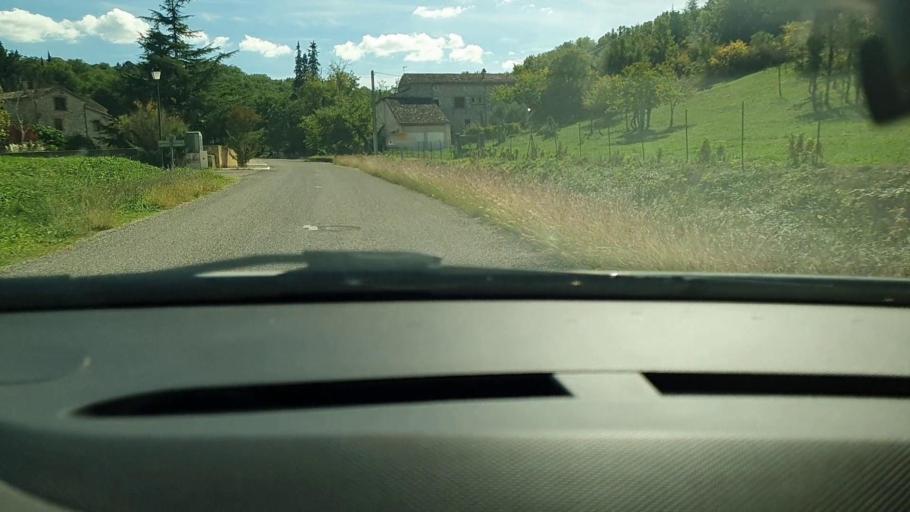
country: FR
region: Languedoc-Roussillon
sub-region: Departement du Gard
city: Saint-Ambroix
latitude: 44.2294
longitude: 4.2817
